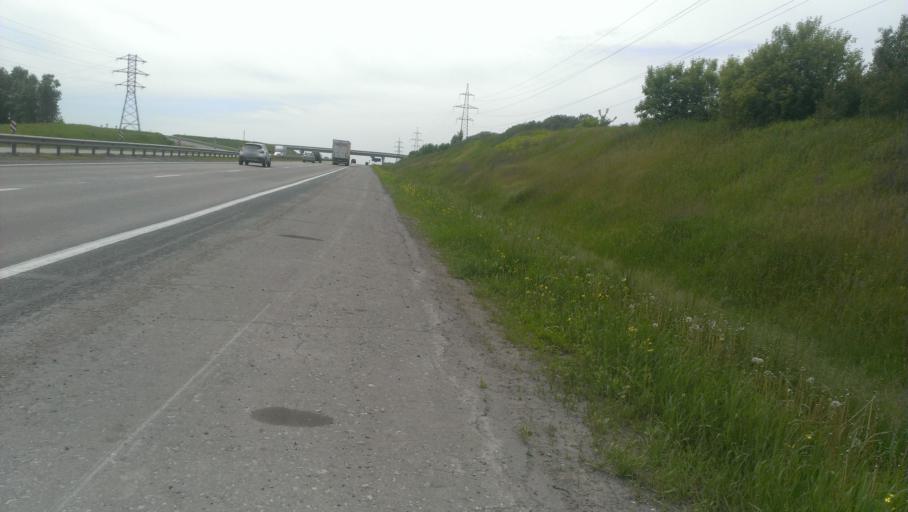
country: RU
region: Altai Krai
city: Sannikovo
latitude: 53.3438
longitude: 83.9406
